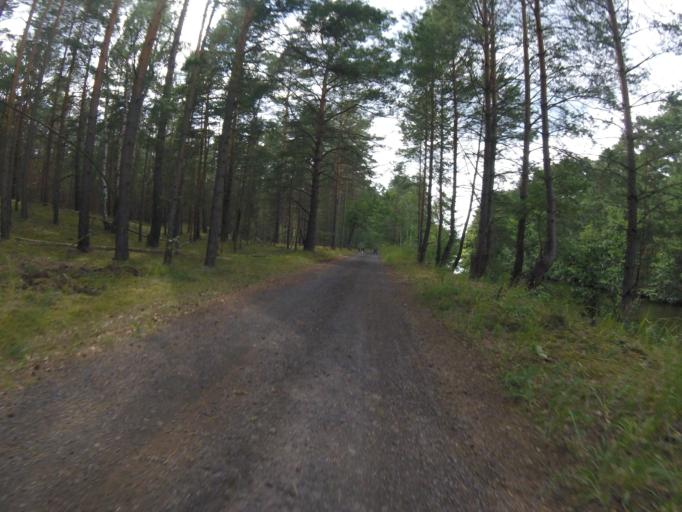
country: DE
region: Brandenburg
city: Munchehofe
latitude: 52.0960
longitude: 13.7856
